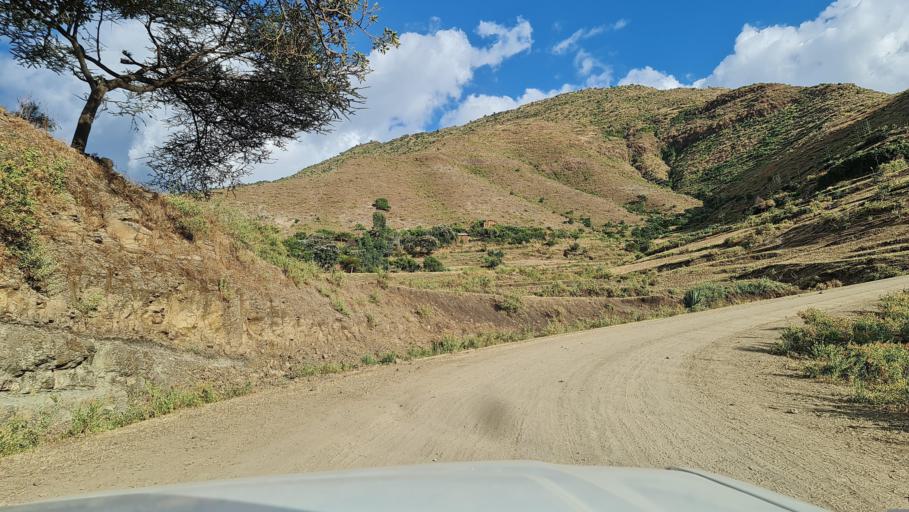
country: ET
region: Amhara
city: Debark'
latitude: 13.0575
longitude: 38.0187
